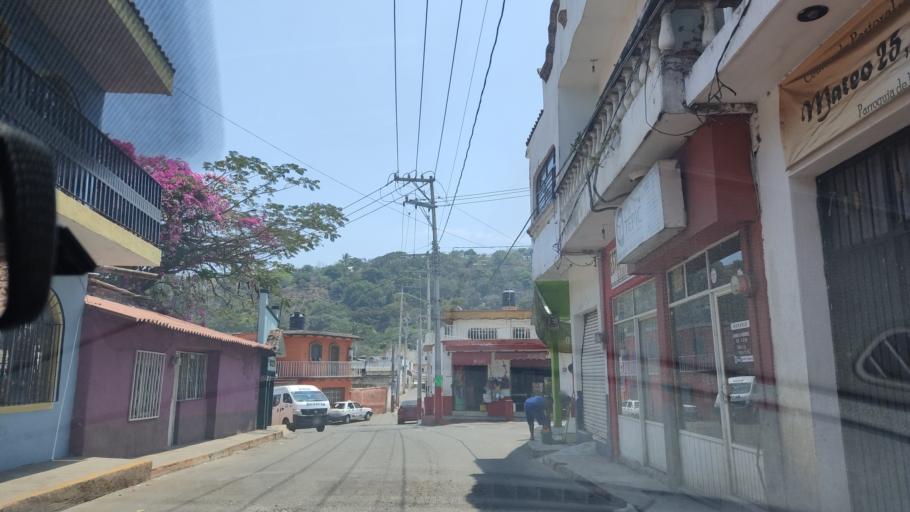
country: MX
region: Nayarit
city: Puga
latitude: 21.5835
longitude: -104.8218
